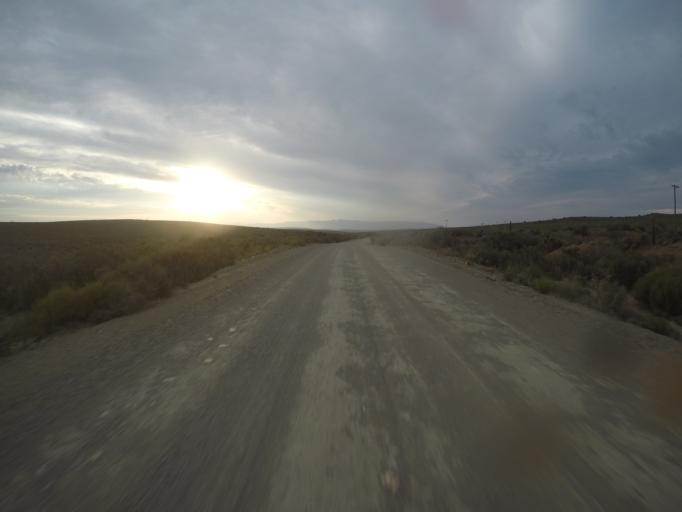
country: ZA
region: Eastern Cape
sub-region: Cacadu District Municipality
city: Willowmore
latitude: -33.5853
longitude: 23.1840
